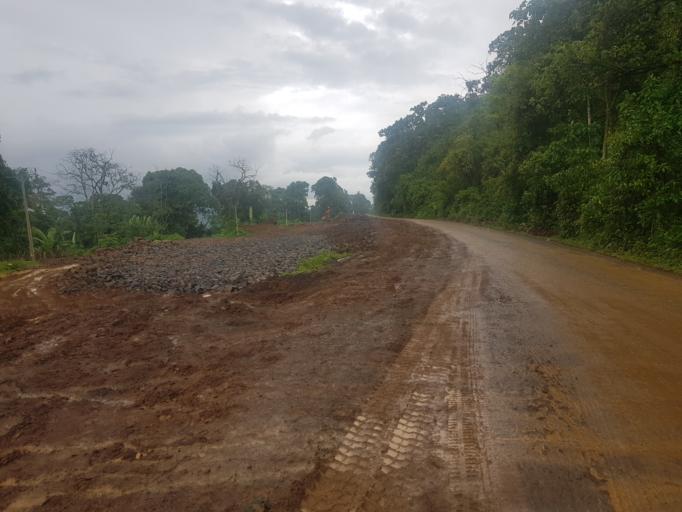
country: ET
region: Oromiya
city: Gore
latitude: 7.6981
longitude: 35.4936
